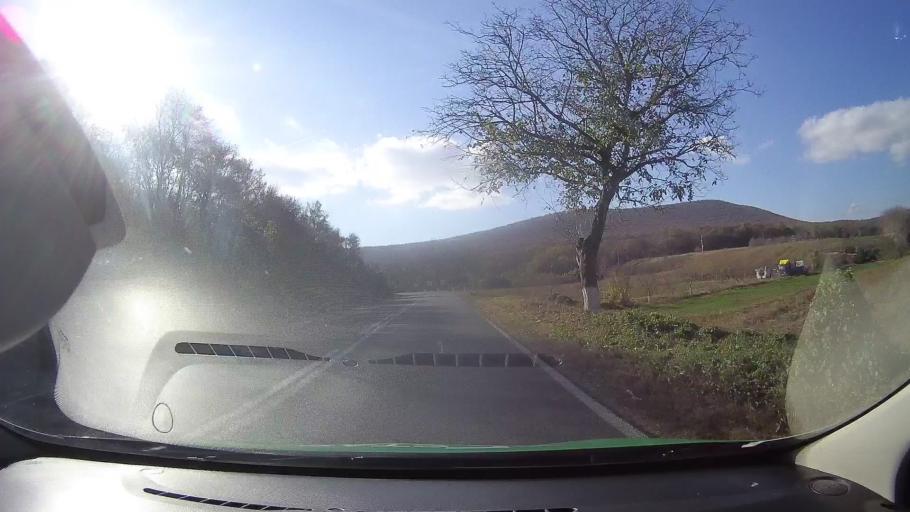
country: RO
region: Tulcea
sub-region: Oras Babadag
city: Babadag
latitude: 44.8750
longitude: 28.6898
